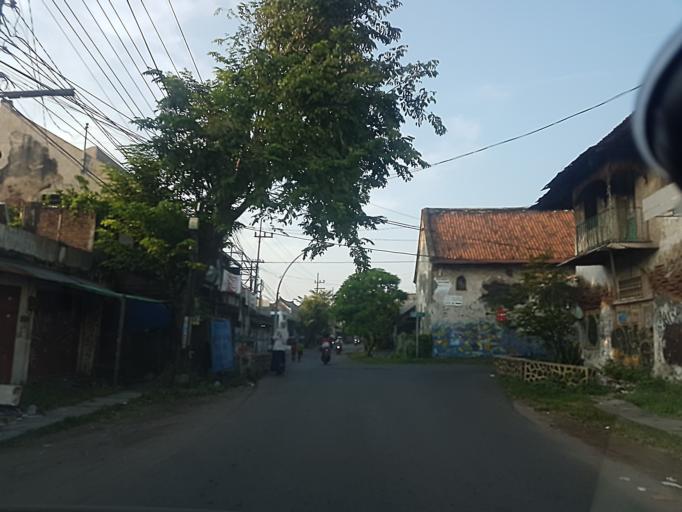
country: ID
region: East Java
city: Gresik
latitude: -7.1564
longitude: 112.6582
